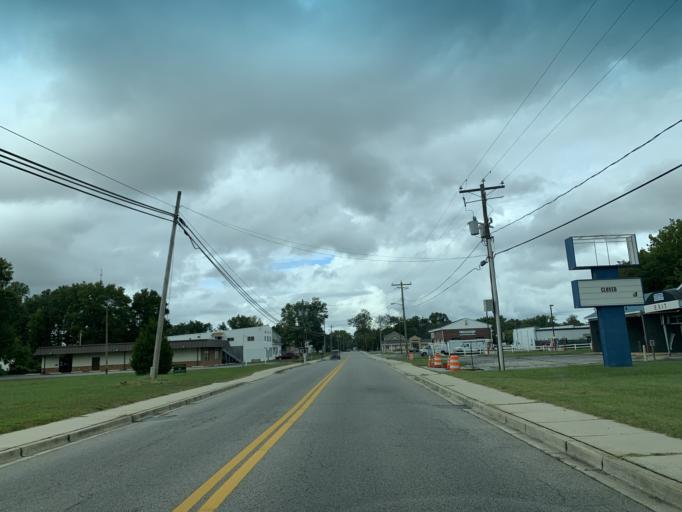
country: US
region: Maryland
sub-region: Caroline County
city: Denton
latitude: 38.8781
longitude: -75.8278
